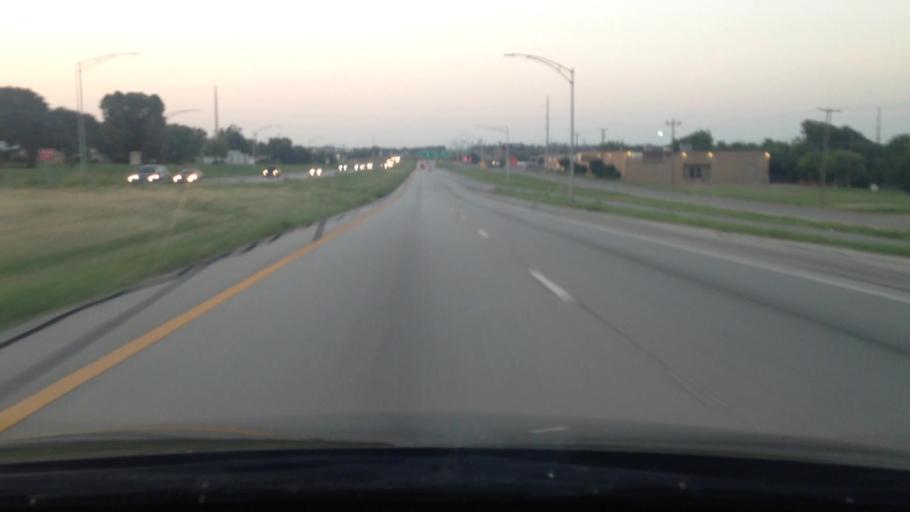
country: US
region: Texas
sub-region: Tarrant County
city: Forest Hill
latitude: 32.7220
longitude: -97.2251
